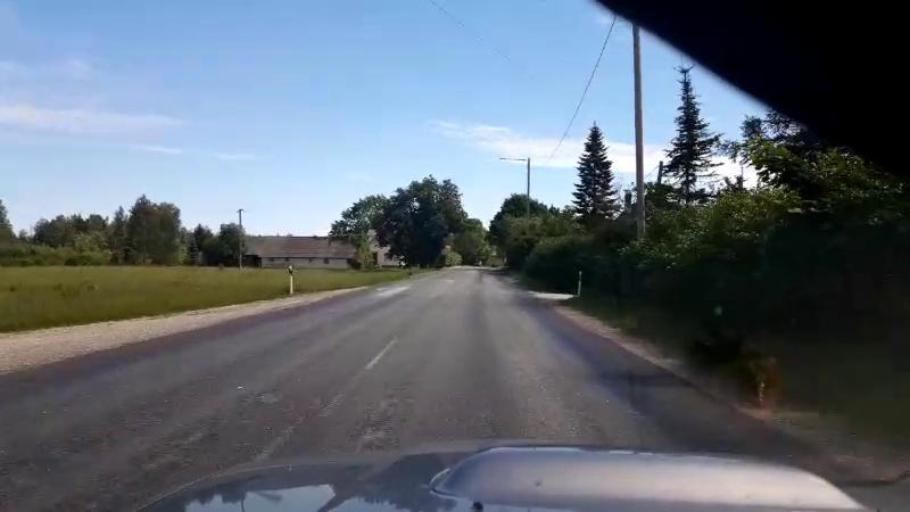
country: EE
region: Laeaene-Virumaa
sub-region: Rakke vald
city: Rakke
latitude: 58.9112
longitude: 26.2743
